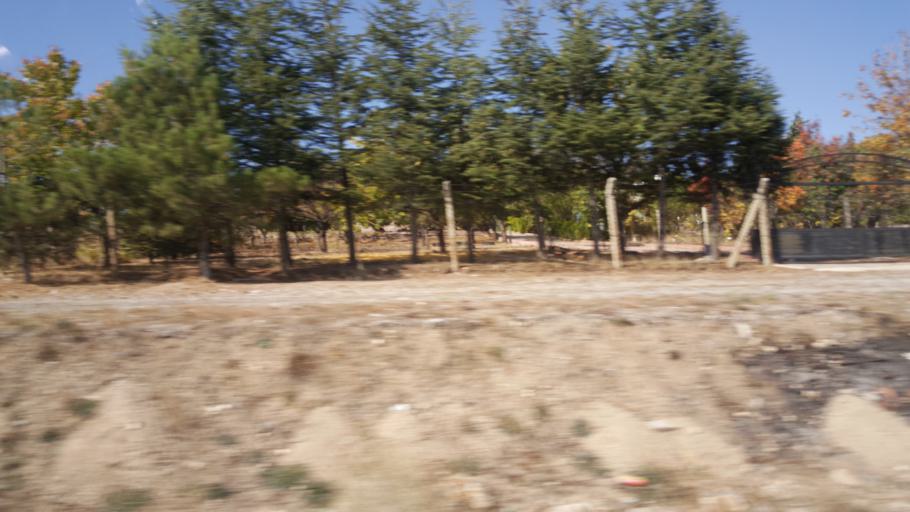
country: TR
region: Ankara
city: Ikizce
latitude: 39.6379
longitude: 32.7147
